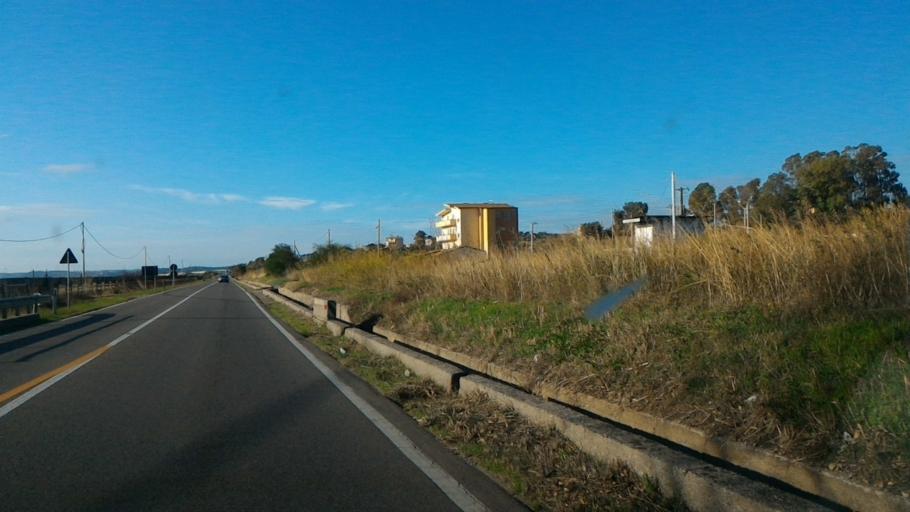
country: IT
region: Calabria
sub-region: Provincia di Crotone
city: Tronca
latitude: 39.1757
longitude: 17.1048
